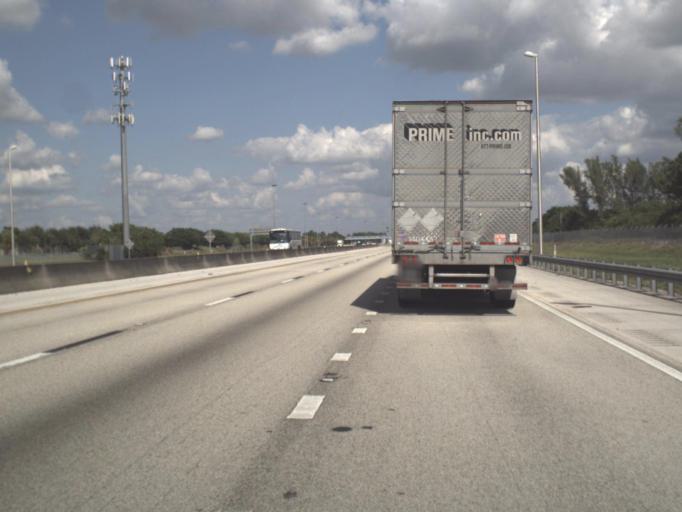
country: US
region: Florida
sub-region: Palm Beach County
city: Seminole Manor
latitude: 26.5546
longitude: -80.1728
